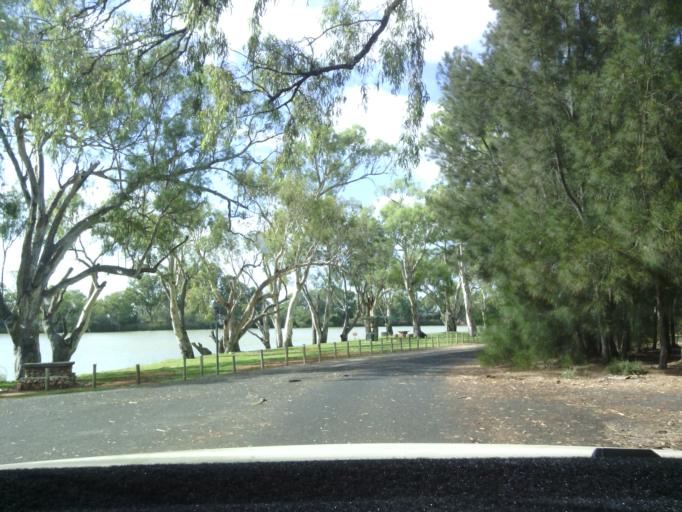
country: AU
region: South Australia
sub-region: Berri and Barmera
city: Berri
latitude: -34.2880
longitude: 140.6318
